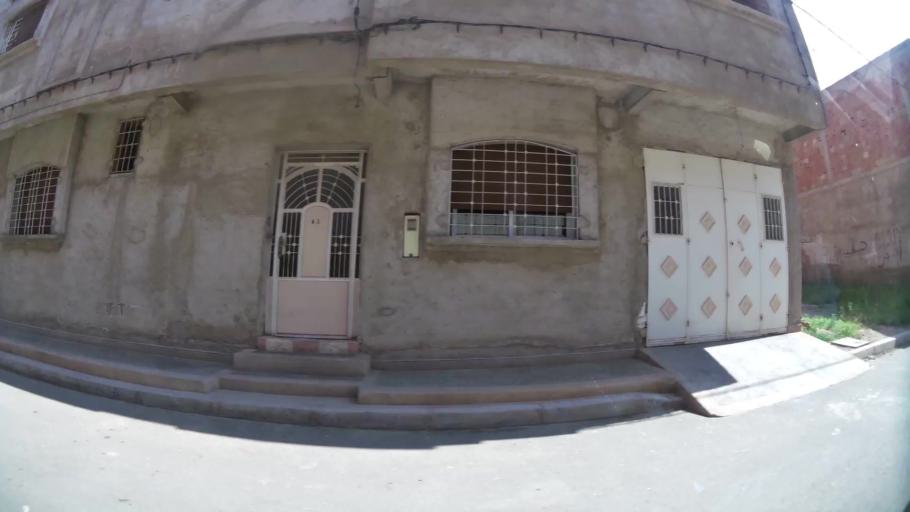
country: MA
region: Oriental
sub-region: Oujda-Angad
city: Oujda
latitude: 34.6911
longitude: -1.8718
